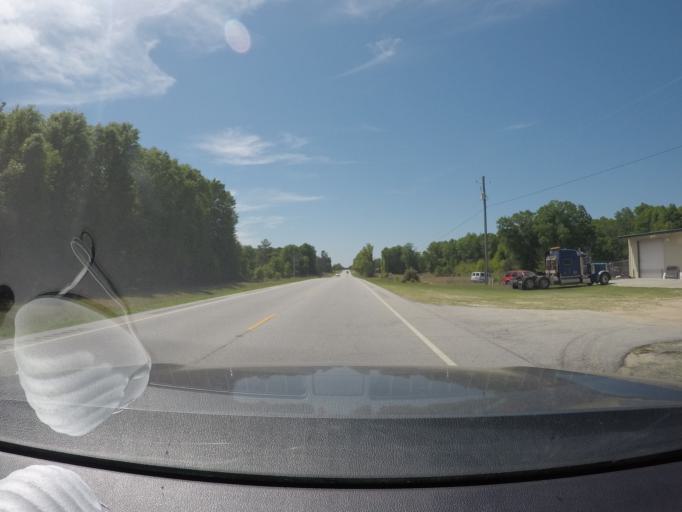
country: US
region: Georgia
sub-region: Bryan County
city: Pembroke
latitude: 32.1459
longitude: -81.7583
